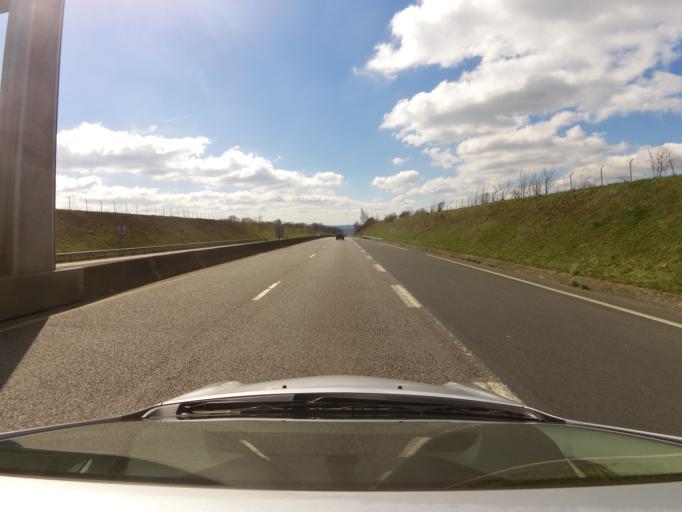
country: FR
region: Haute-Normandie
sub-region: Departement de la Seine-Maritime
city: Neufchatel-en-Bray
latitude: 49.7402
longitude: 1.4716
